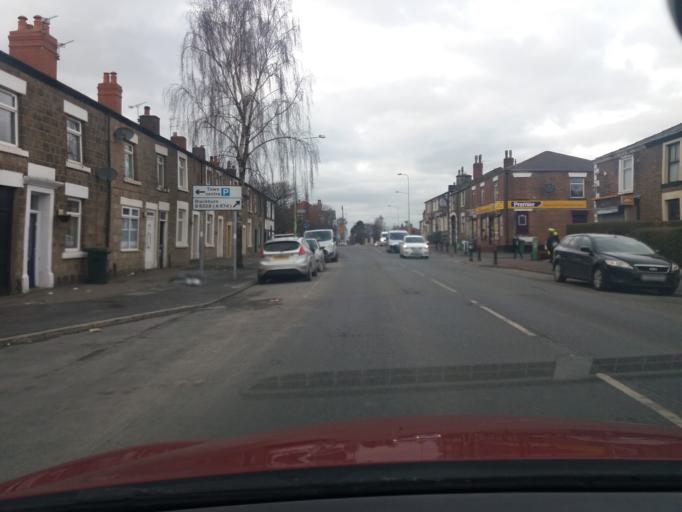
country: GB
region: England
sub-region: Lancashire
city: Chorley
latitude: 53.6518
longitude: -2.6177
